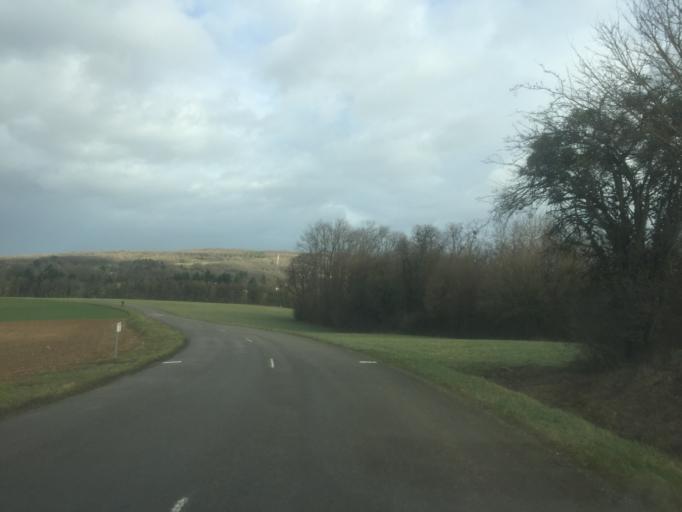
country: FR
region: Franche-Comte
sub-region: Departement du Jura
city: Orchamps
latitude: 47.2135
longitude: 5.6832
